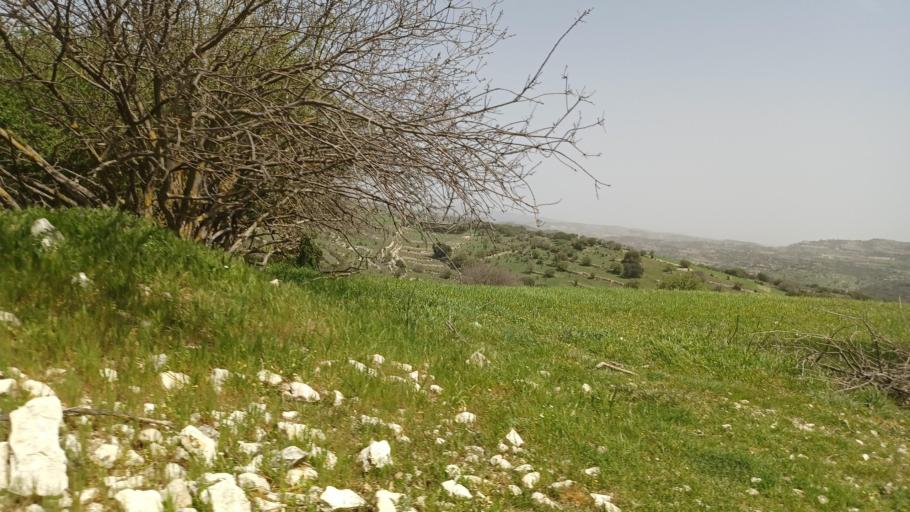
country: CY
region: Limassol
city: Pachna
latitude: 34.7829
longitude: 32.7502
